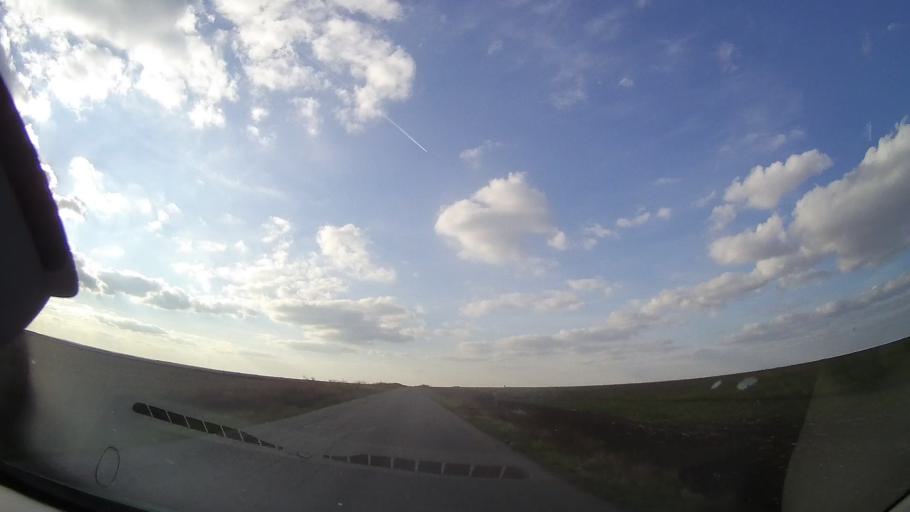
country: RO
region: Constanta
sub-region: Comuna Cerchezu
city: Cerchezu
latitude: 43.8238
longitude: 28.1435
